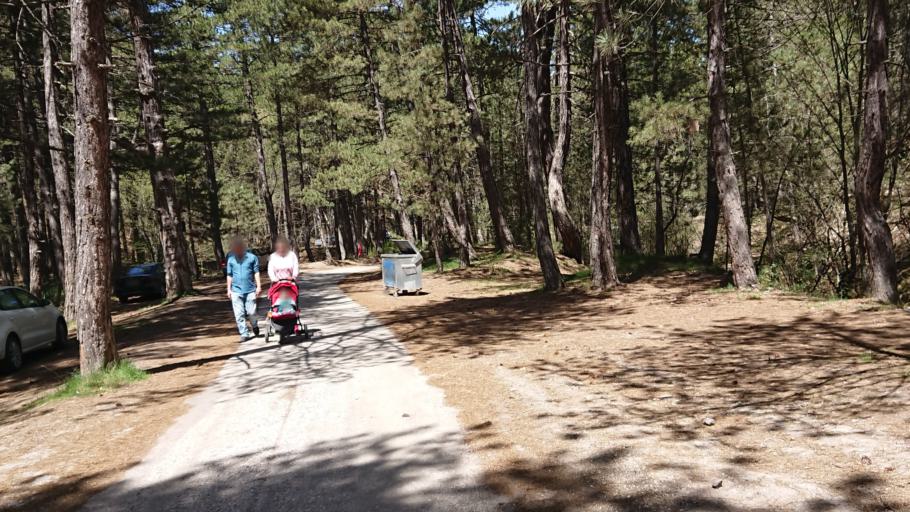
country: TR
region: Kuetahya
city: Sabuncu
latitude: 39.5113
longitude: 30.4230
